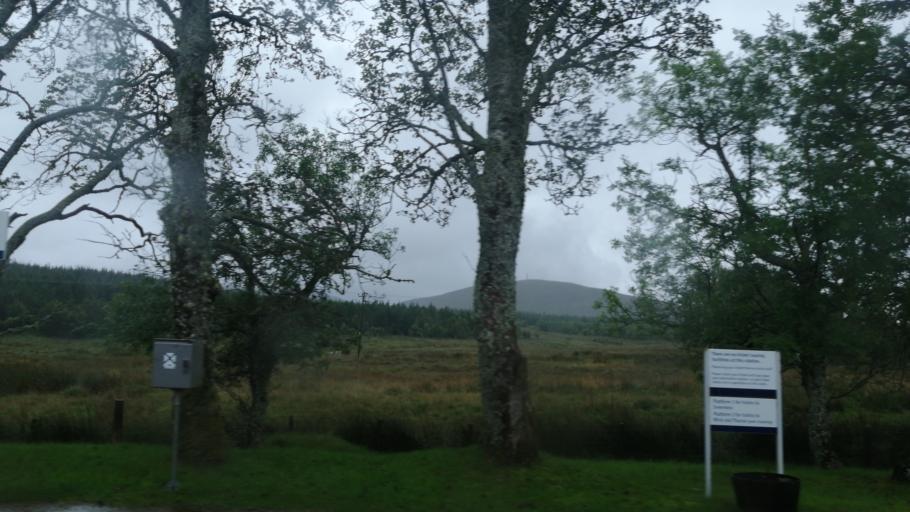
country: GB
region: Scotland
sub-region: Highland
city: Brora
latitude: 58.3566
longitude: -3.8976
